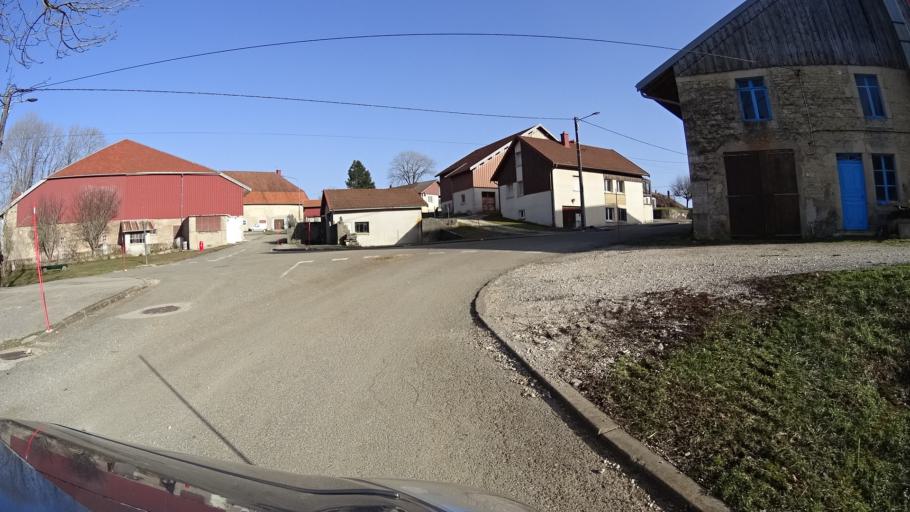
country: FR
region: Franche-Comte
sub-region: Departement du Doubs
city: Frasne
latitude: 46.8950
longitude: 6.2232
